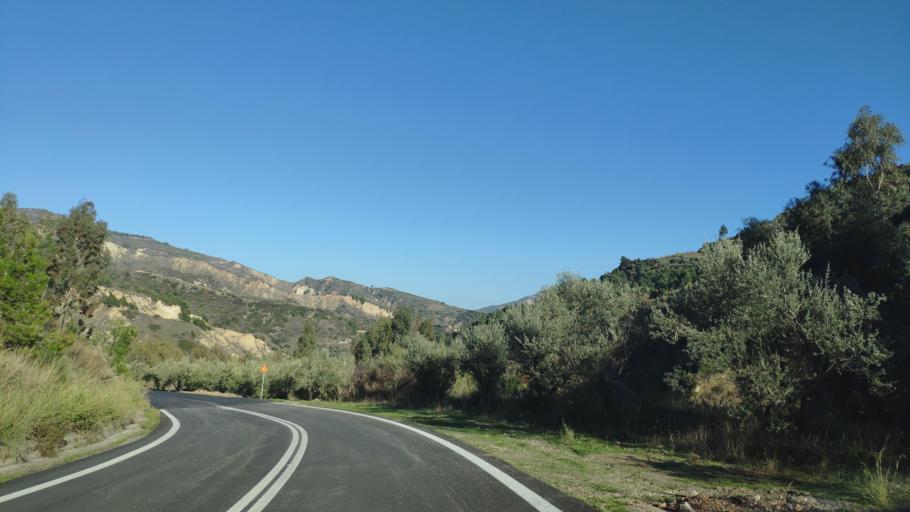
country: GR
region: Peloponnese
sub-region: Nomos Korinthias
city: Xylokastro
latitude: 38.0046
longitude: 22.5124
